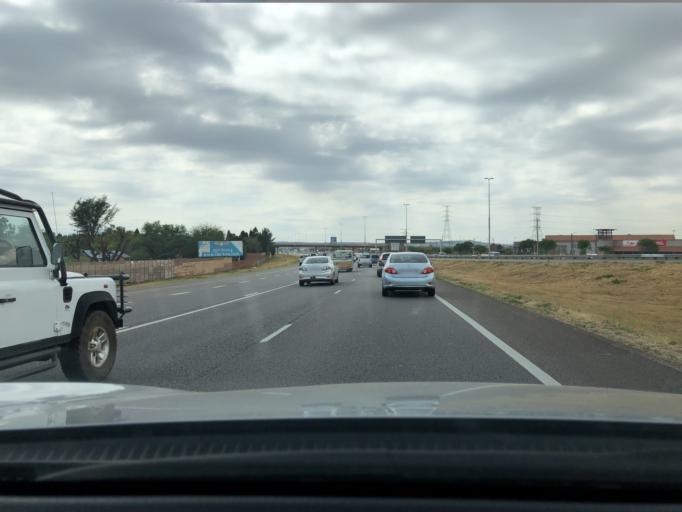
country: ZA
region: Gauteng
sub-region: City of Tshwane Metropolitan Municipality
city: Centurion
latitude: -25.8756
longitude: 28.1725
